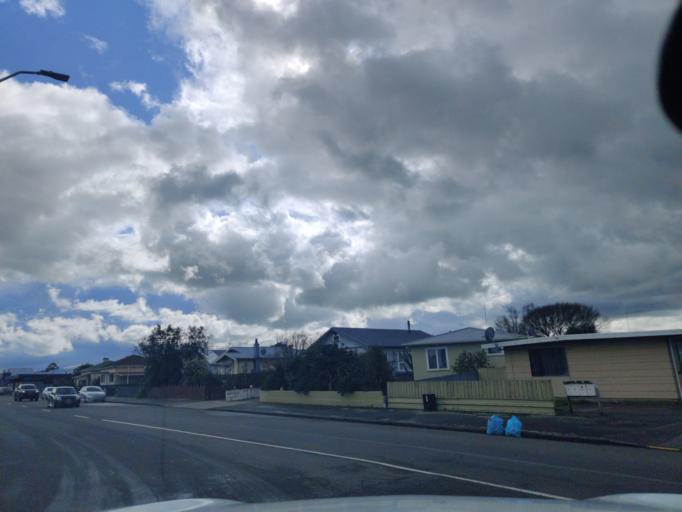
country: NZ
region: Manawatu-Wanganui
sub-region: Palmerston North City
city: Palmerston North
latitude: -40.2305
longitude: 175.5679
